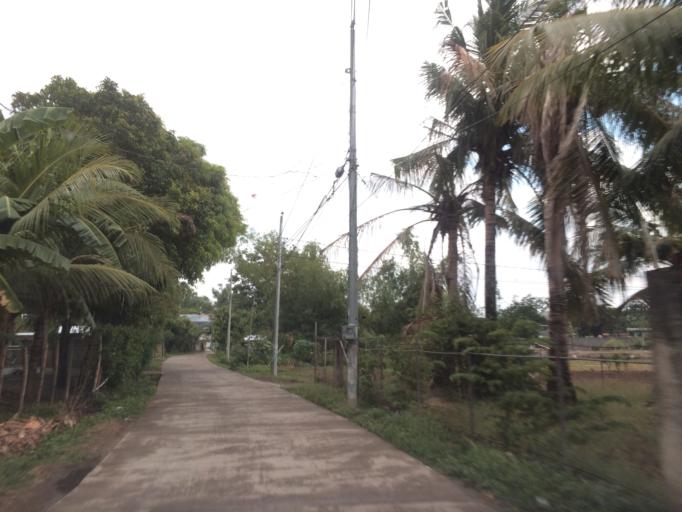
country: PH
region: Ilocos
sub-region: Province of Pangasinan
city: Dumpay
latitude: 15.8789
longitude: 120.3874
